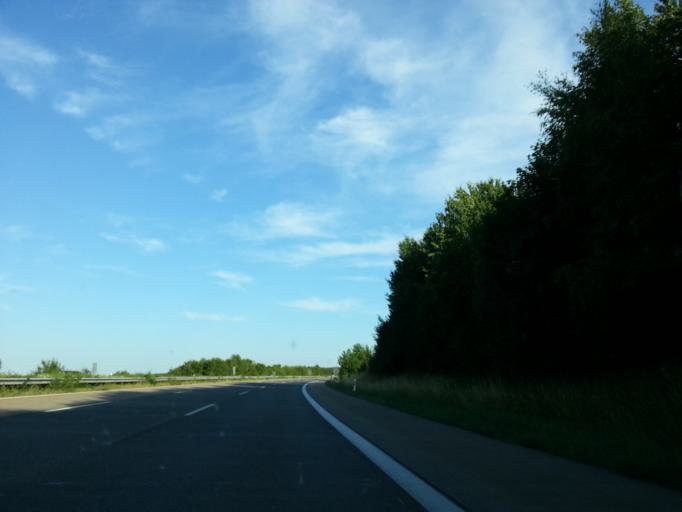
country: DE
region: Rheinland-Pfalz
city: Polich
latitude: 49.7776
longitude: 6.8483
